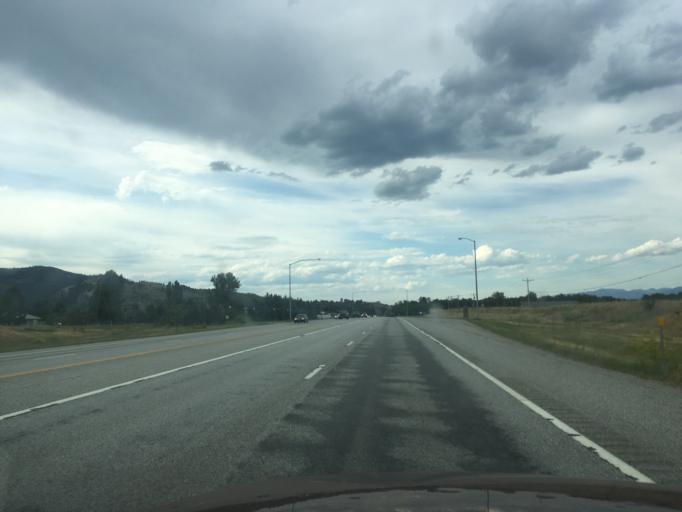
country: US
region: Montana
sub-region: Missoula County
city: Lolo
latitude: 46.7406
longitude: -114.0812
